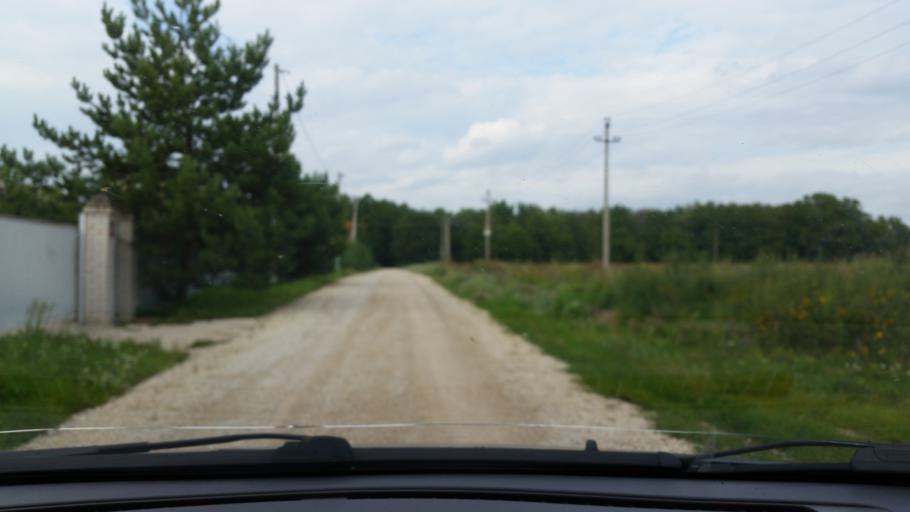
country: RU
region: Moskovskaya
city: Bol'shoye Gryzlovo
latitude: 54.8504
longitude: 37.7024
